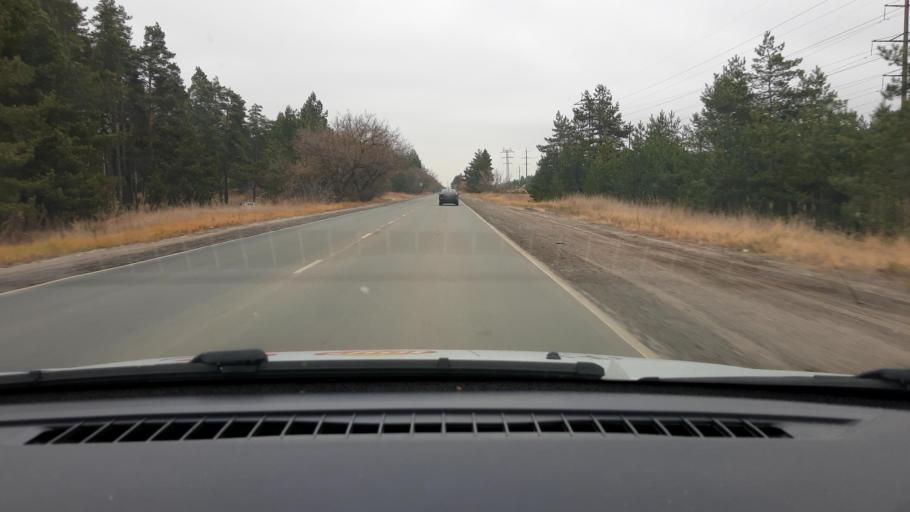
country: RU
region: Nizjnij Novgorod
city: Dzerzhinsk
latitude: 56.2557
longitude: 43.4372
